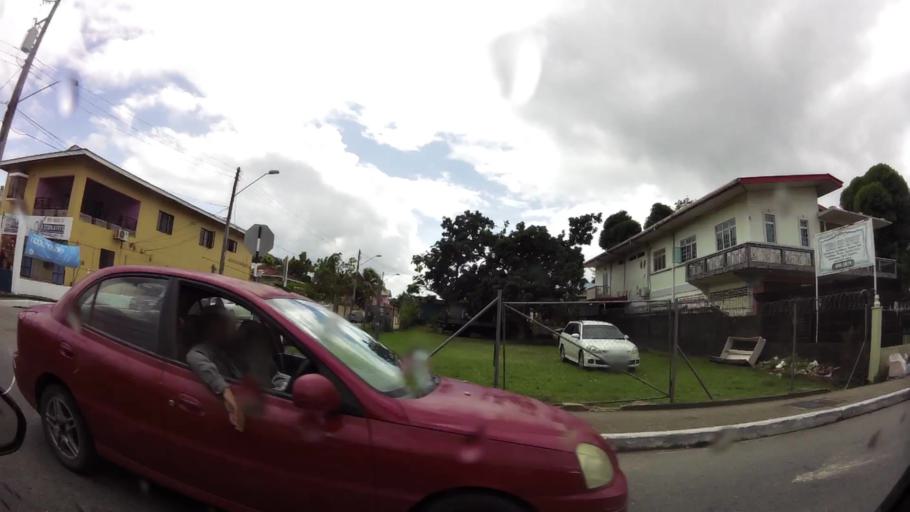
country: TT
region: Tunapuna/Piarco
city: Arouca
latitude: 10.6338
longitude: -61.3371
